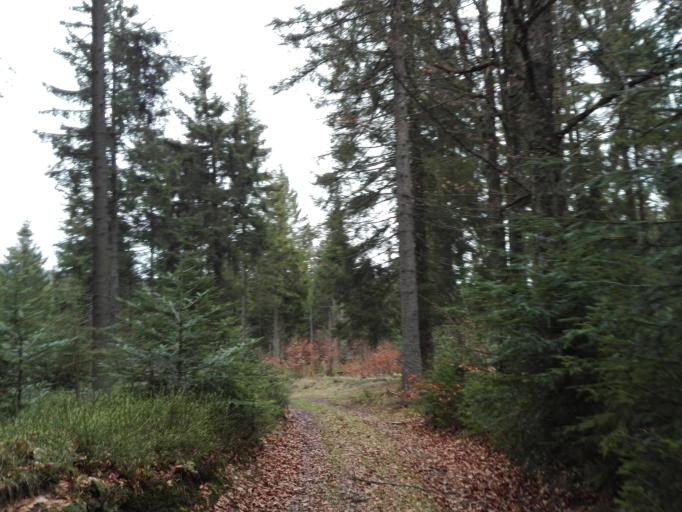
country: AT
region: Upper Austria
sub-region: Politischer Bezirk Rohrbach
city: Ulrichsberg
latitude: 48.7009
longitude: 13.9532
